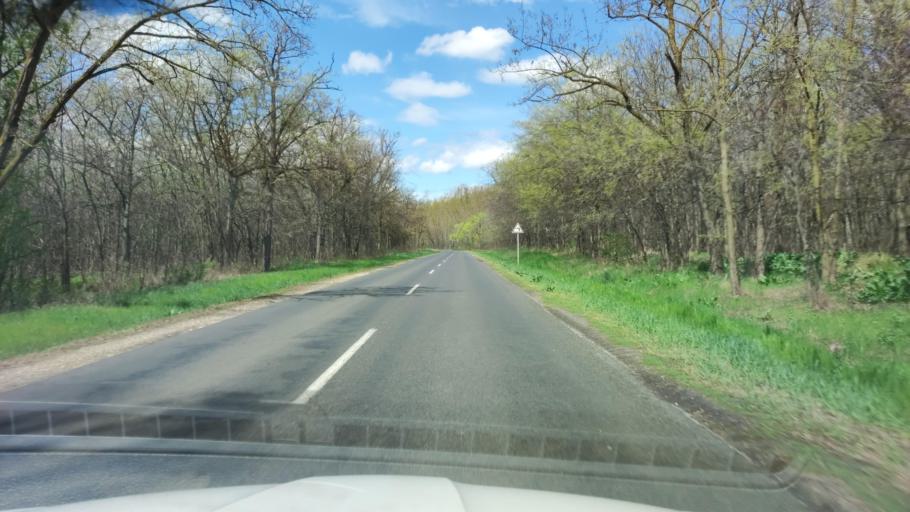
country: HU
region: Pest
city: Cegled
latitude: 47.1508
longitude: 19.8635
